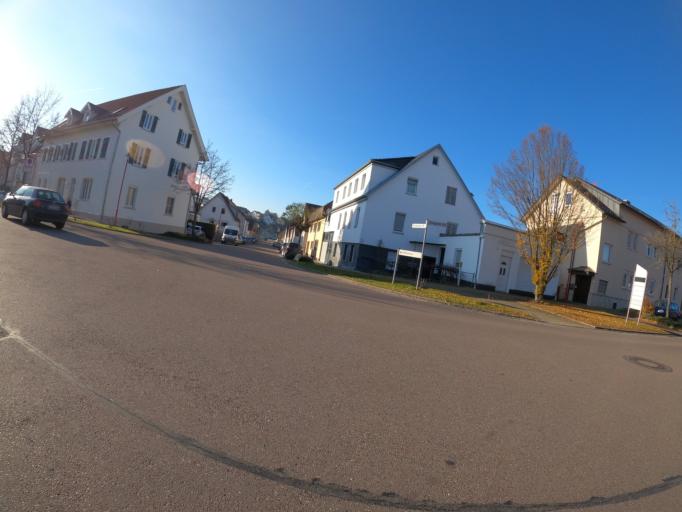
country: DE
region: Baden-Wuerttemberg
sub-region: Regierungsbezirk Stuttgart
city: Uhingen
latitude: 48.7064
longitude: 9.5808
